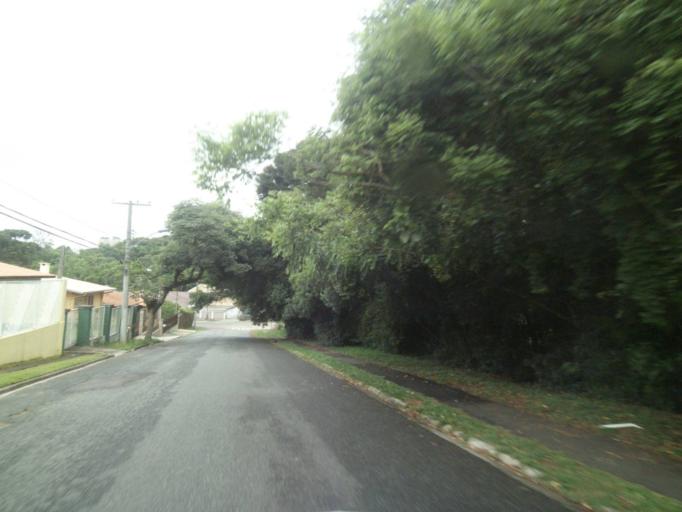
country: BR
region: Parana
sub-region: Curitiba
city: Curitiba
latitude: -25.4289
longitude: -49.3420
